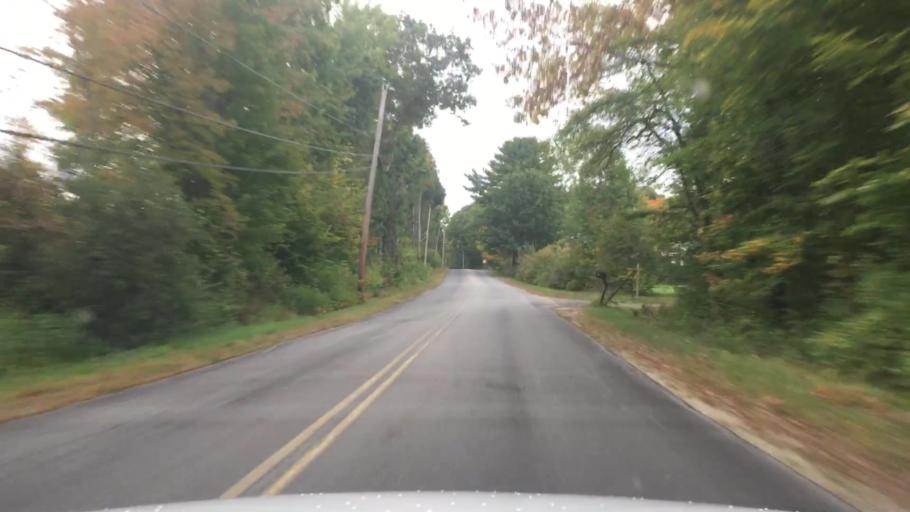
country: US
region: Maine
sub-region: York County
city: Buxton
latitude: 43.6187
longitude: -70.5414
